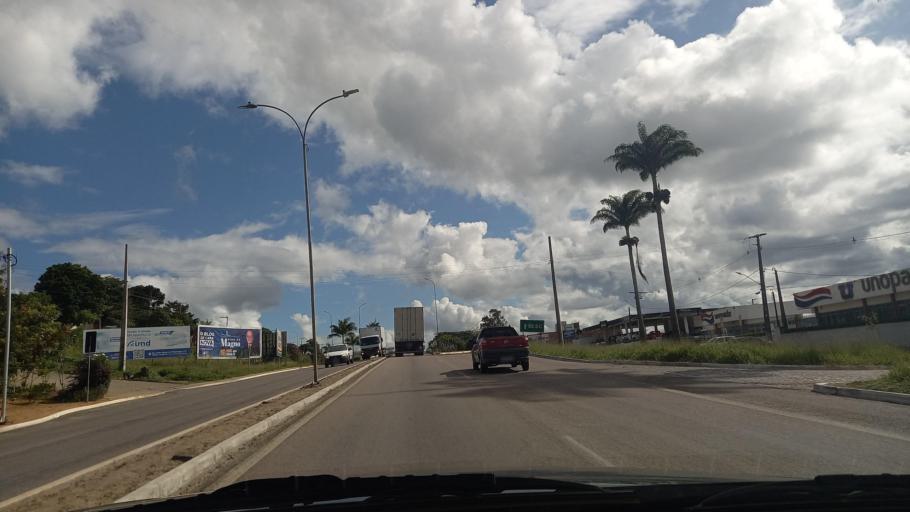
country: BR
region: Pernambuco
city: Garanhuns
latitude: -8.8754
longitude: -36.4718
